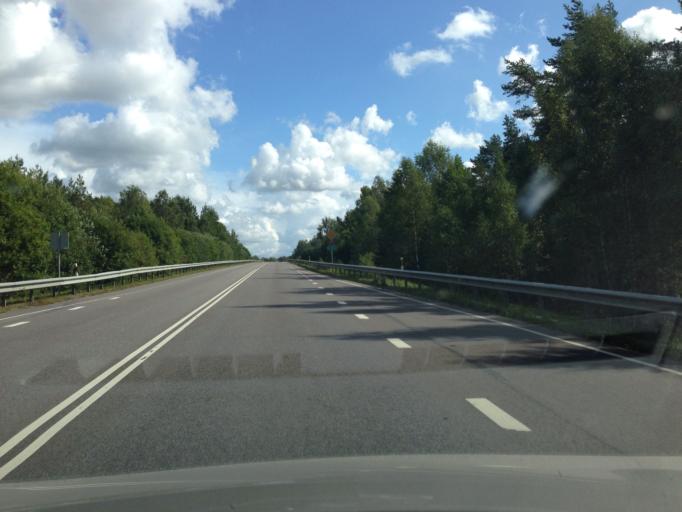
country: EE
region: Harju
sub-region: Saku vald
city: Saku
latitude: 59.3149
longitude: 24.6790
